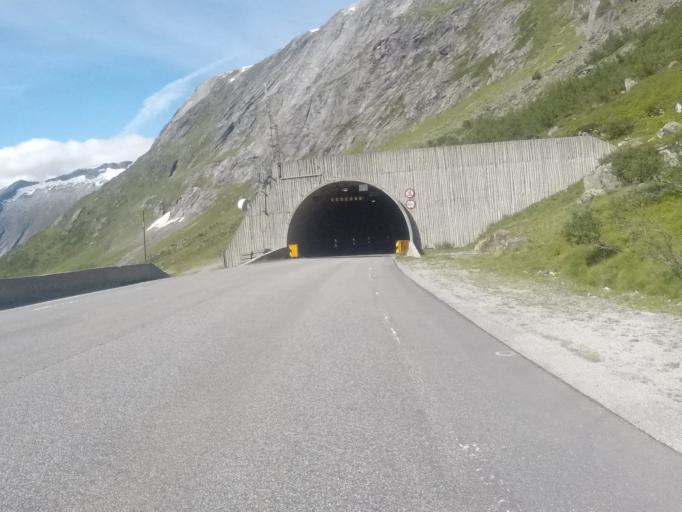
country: NO
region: More og Romsdal
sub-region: Norddal
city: Valldal
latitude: 61.9860
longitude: 7.3062
